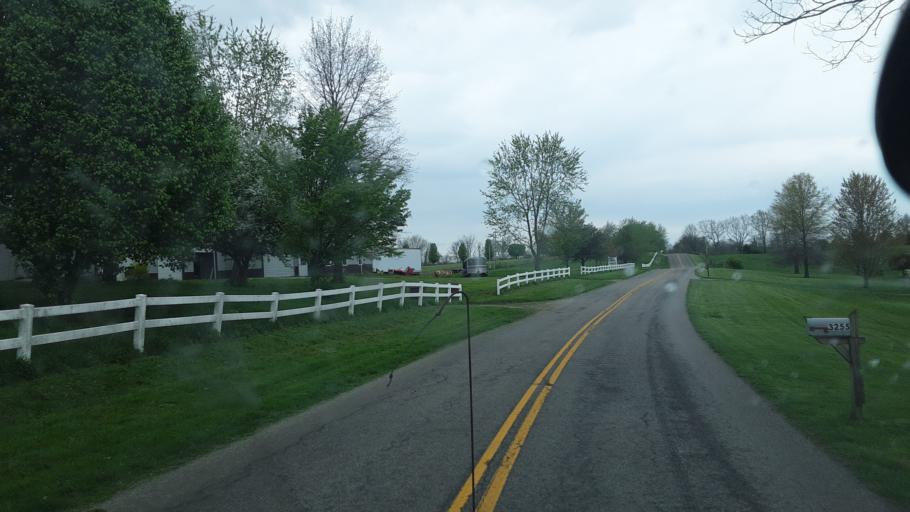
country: US
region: Kentucky
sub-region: Owen County
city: Owenton
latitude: 38.6139
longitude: -84.7864
